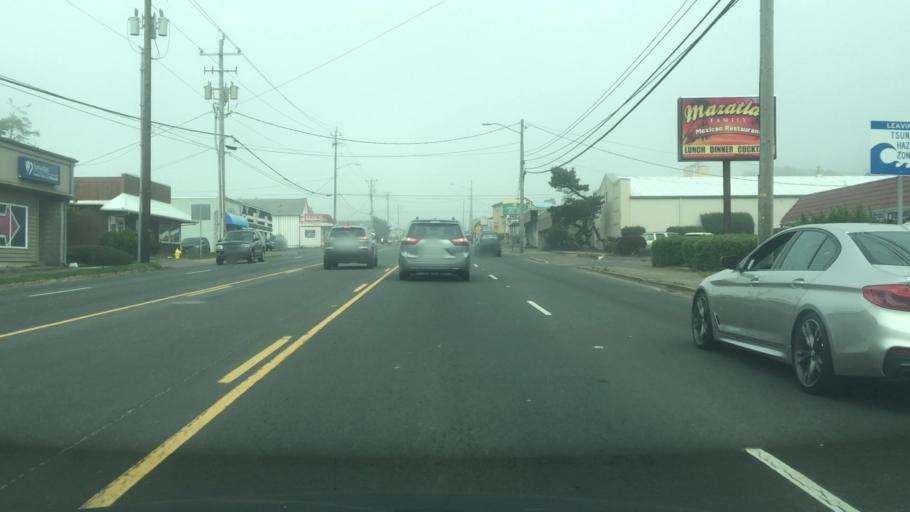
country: US
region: Oregon
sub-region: Lincoln County
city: Lincoln City
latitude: 44.9717
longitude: -124.0143
